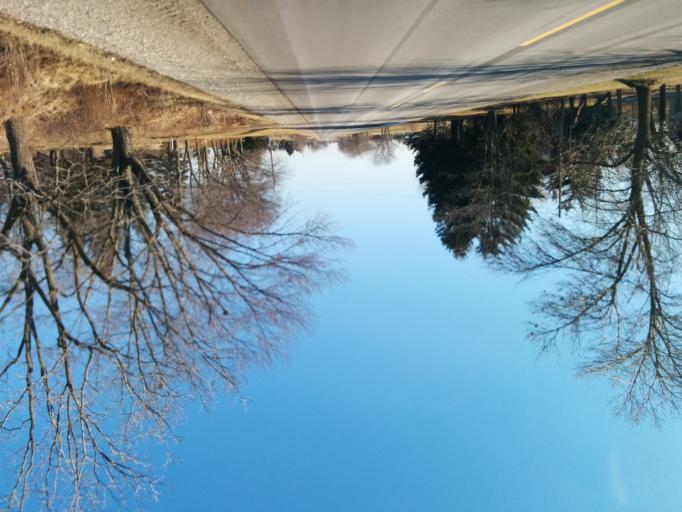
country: CA
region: Ontario
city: Brantford
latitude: 43.0364
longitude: -80.3010
